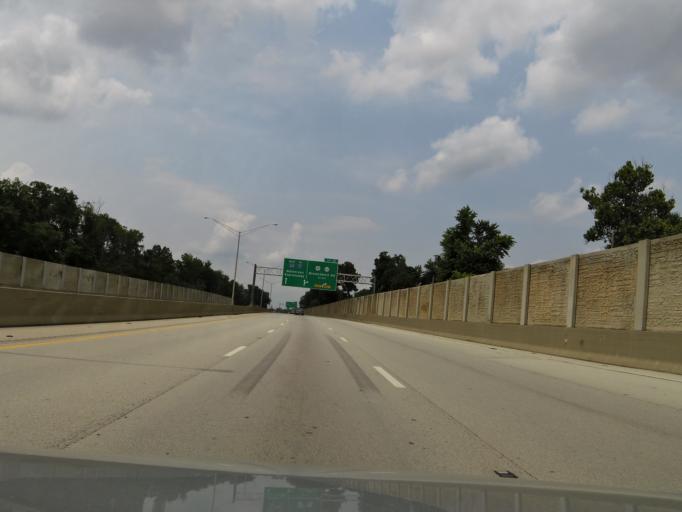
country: US
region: Kentucky
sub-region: Jefferson County
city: Graymoor-Devondale
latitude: 38.2706
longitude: -85.6274
